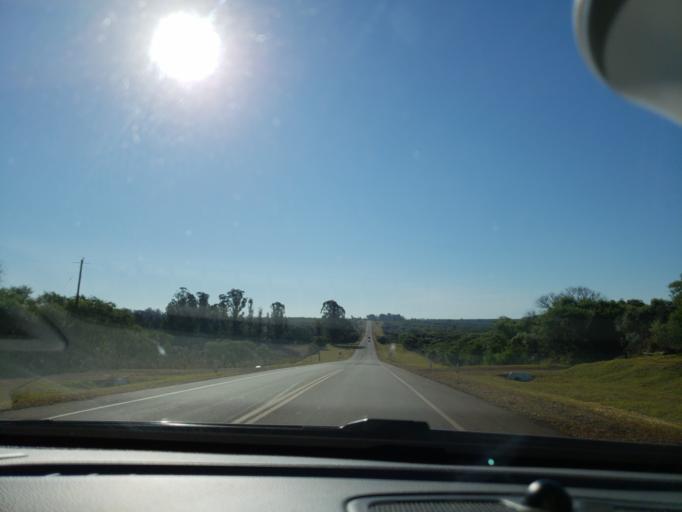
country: AR
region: Misiones
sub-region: Departamento de Apostoles
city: Apostoles
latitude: -27.8505
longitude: -55.7636
